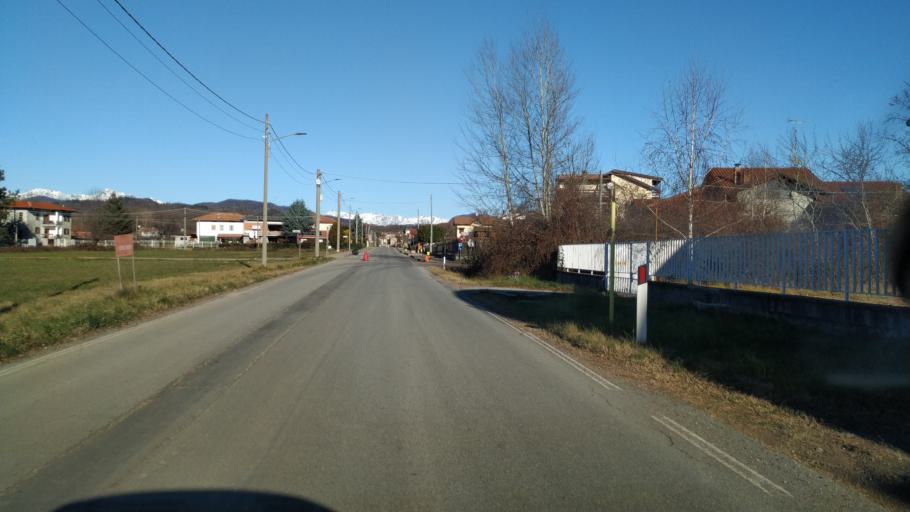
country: IT
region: Piedmont
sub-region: Provincia di Vercelli
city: Lozzolo
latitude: 45.6110
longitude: 8.3245
